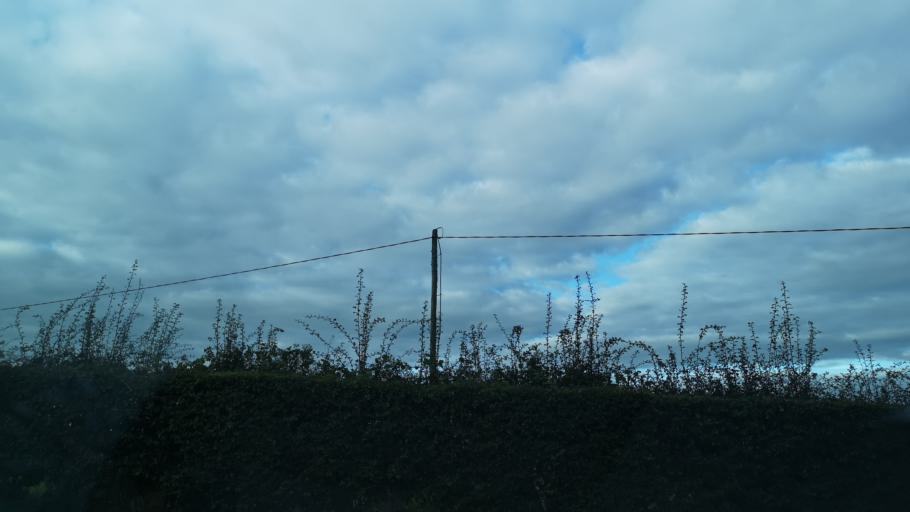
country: IE
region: Connaught
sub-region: County Galway
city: Loughrea
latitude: 53.1501
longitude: -8.4913
